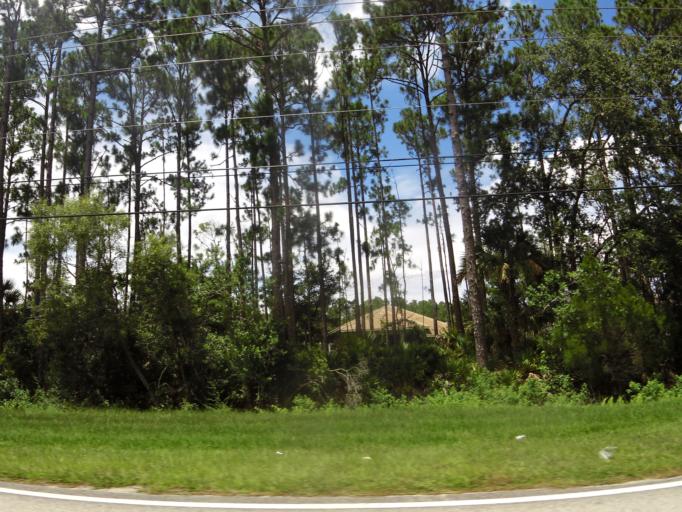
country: US
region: Florida
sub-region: Flagler County
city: Flagler Beach
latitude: 29.4037
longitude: -81.1622
